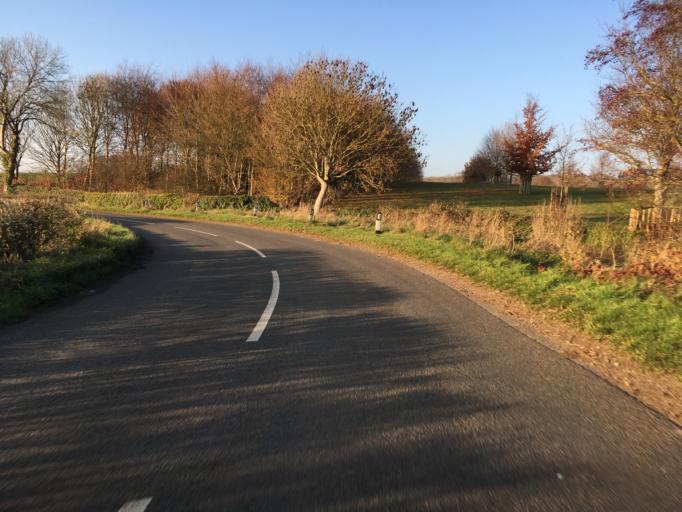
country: GB
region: England
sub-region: Wiltshire
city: Luckington
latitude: 51.5637
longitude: -2.2884
